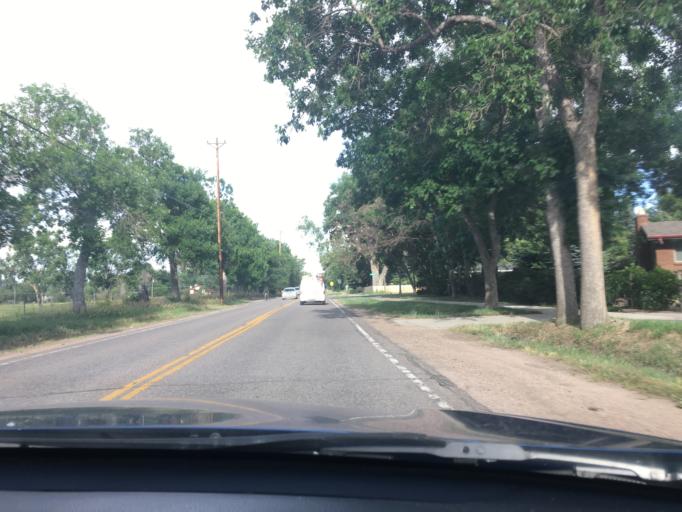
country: US
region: Colorado
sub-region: Jefferson County
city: Applewood
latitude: 39.7618
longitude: -105.1552
